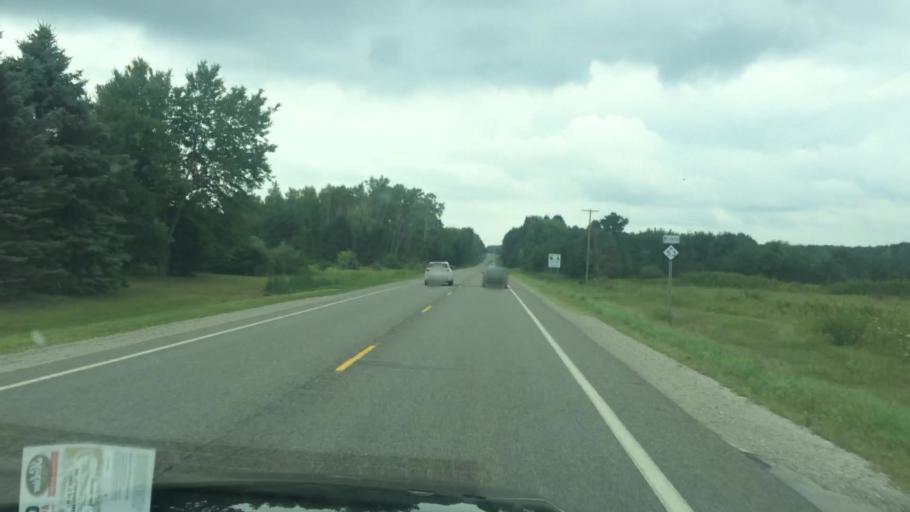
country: US
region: Michigan
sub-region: Tuscola County
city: Cass City
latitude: 43.6177
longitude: -83.0969
